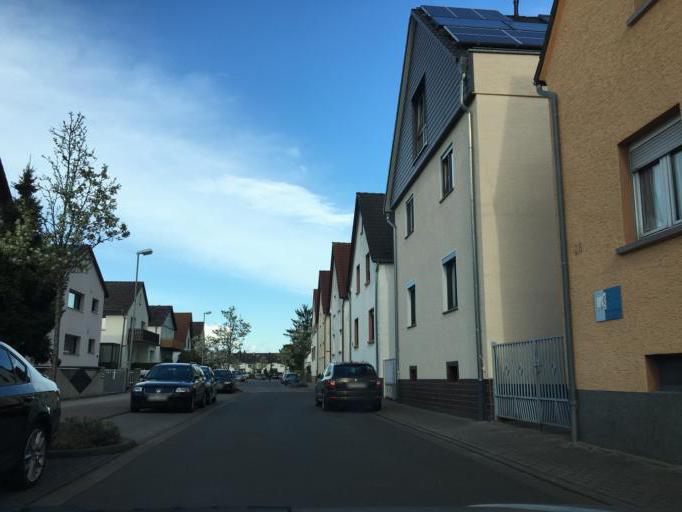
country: DE
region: Hesse
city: Obertshausen
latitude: 50.0849
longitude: 8.8604
